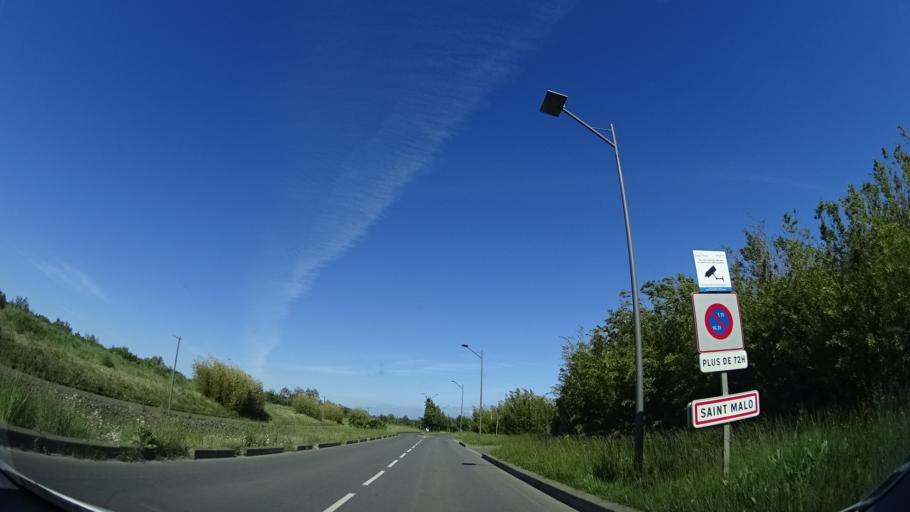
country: FR
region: Brittany
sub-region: Departement d'Ille-et-Vilaine
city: Saint-Jouan-des-Guerets
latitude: 48.6139
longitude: -1.9792
